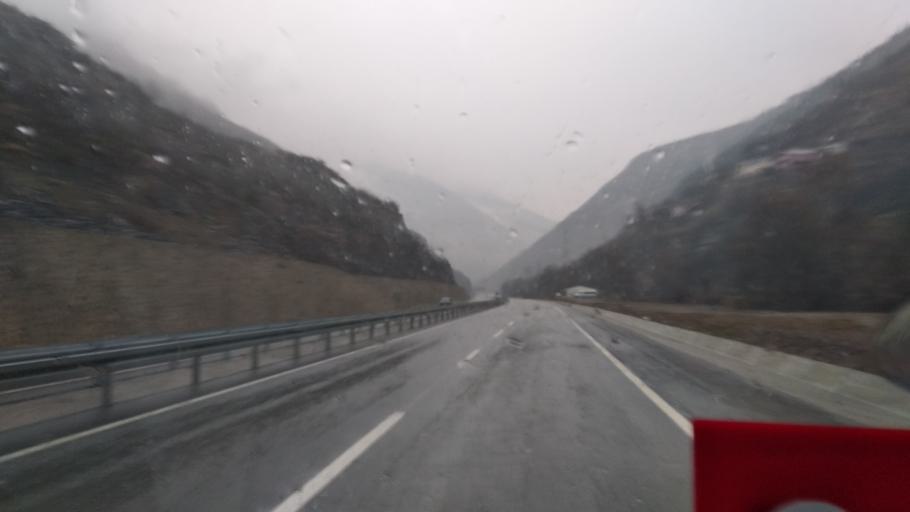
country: TR
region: Trabzon
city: Macka
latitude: 40.7876
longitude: 39.5785
